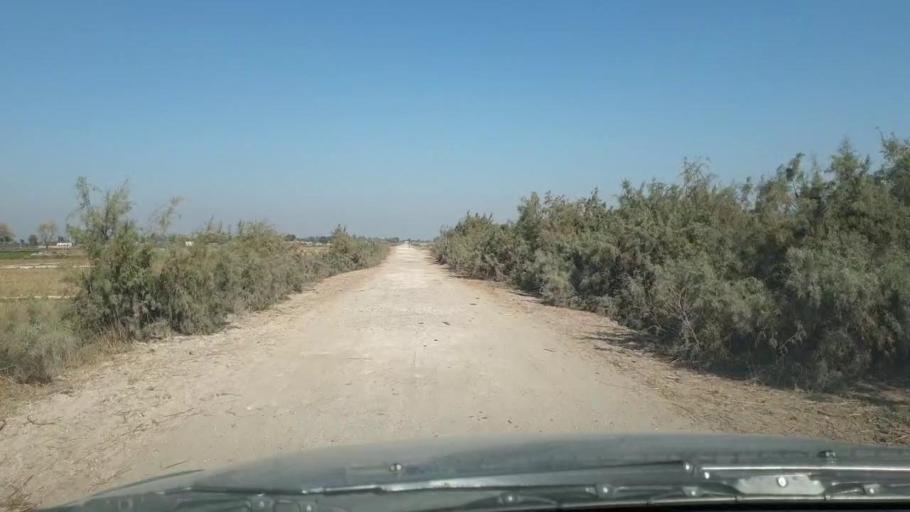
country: PK
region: Sindh
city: Adilpur
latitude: 27.8796
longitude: 69.2699
